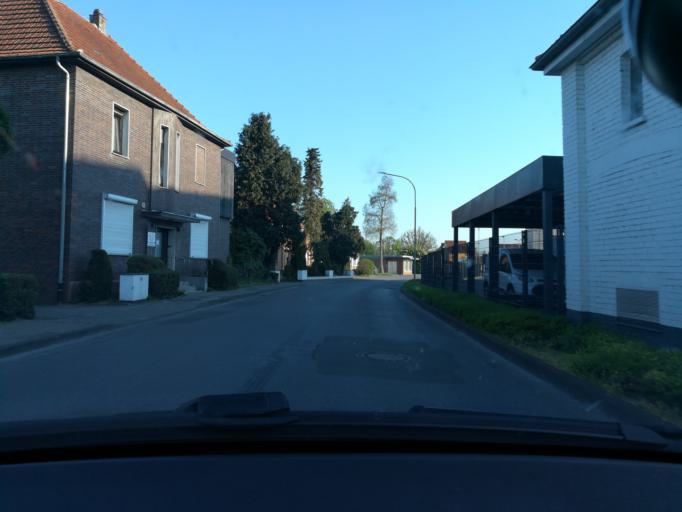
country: DE
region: North Rhine-Westphalia
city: Versmold
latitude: 52.0416
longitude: 8.1475
